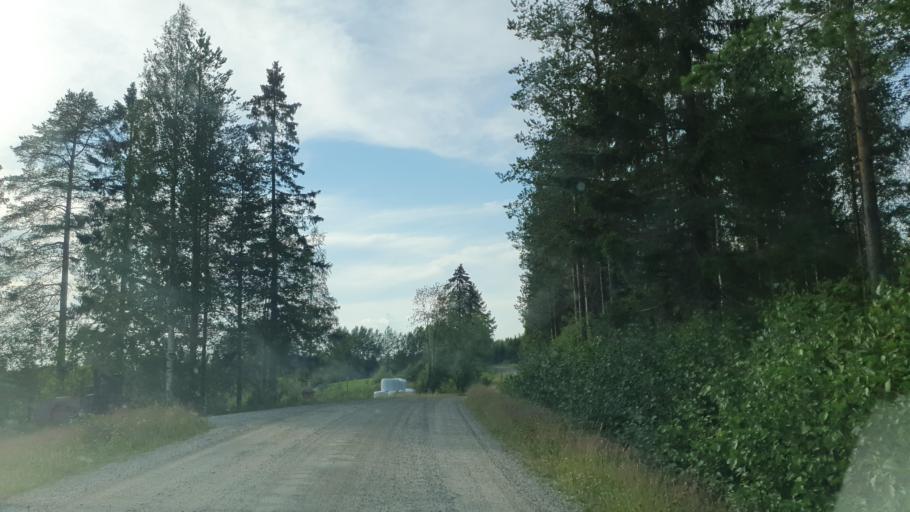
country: FI
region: Kainuu
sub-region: Kehys-Kainuu
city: Kuhmo
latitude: 64.2417
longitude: 29.5035
